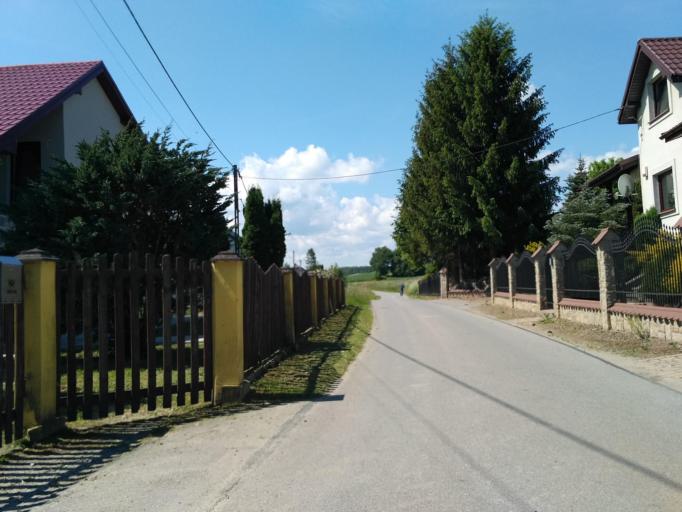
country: PL
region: Subcarpathian Voivodeship
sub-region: Powiat krosnienski
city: Miejsce Piastowe
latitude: 49.6479
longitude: 21.7585
